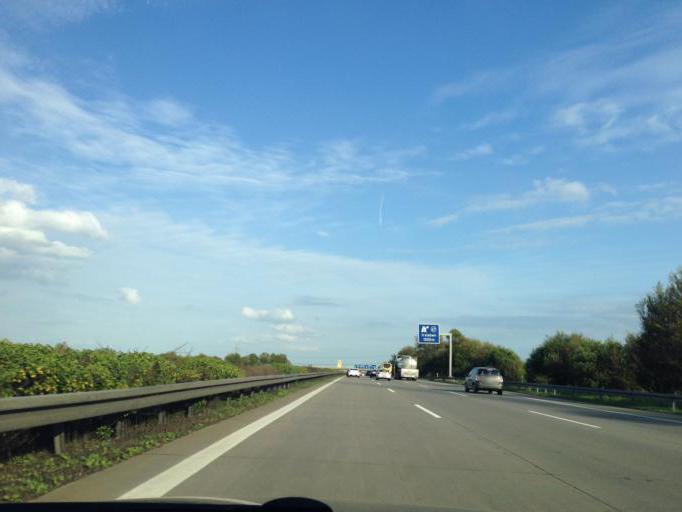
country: DE
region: Saxony-Anhalt
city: Hermsdorf
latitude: 52.1800
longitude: 11.4671
